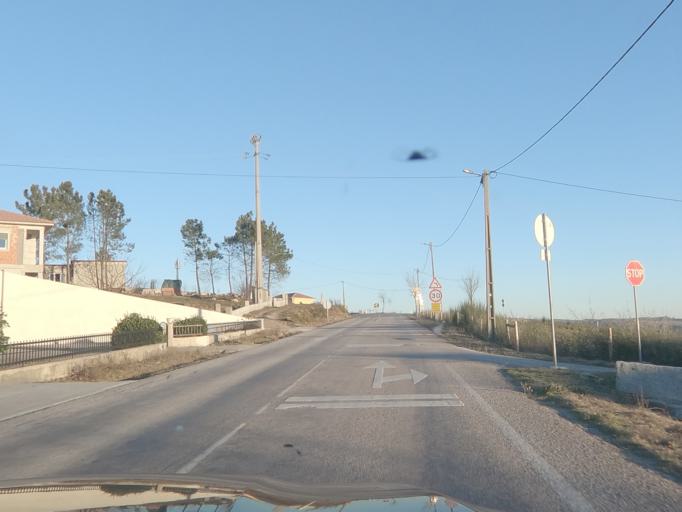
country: PT
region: Vila Real
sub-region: Vila Pouca de Aguiar
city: Vila Pouca de Aguiar
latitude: 41.4952
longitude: -7.7242
